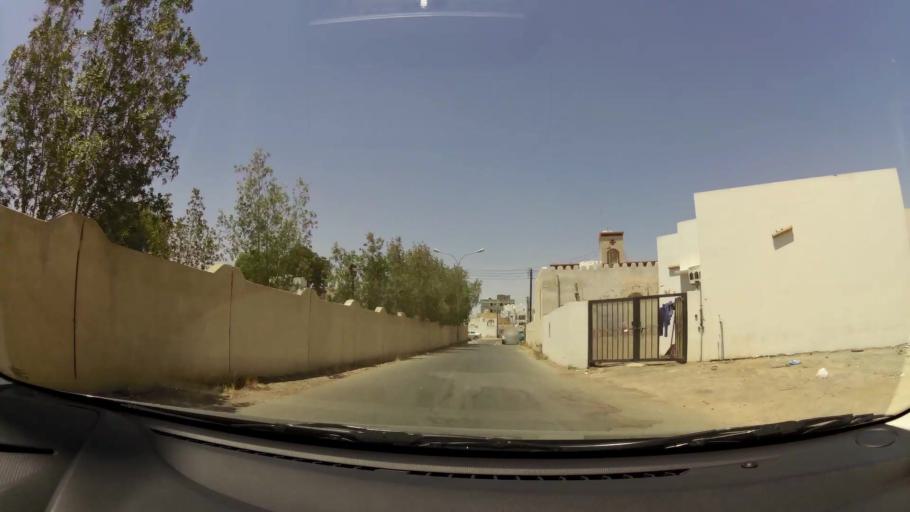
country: OM
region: Muhafazat Masqat
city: As Sib al Jadidah
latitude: 23.6269
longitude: 58.2394
